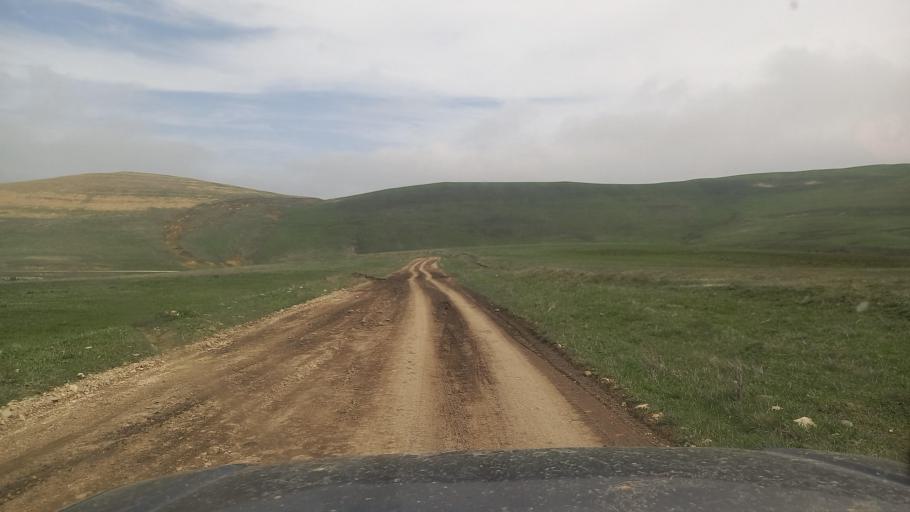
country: RU
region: Stavropol'skiy
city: Kislovodsk
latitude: 43.7700
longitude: 42.8539
